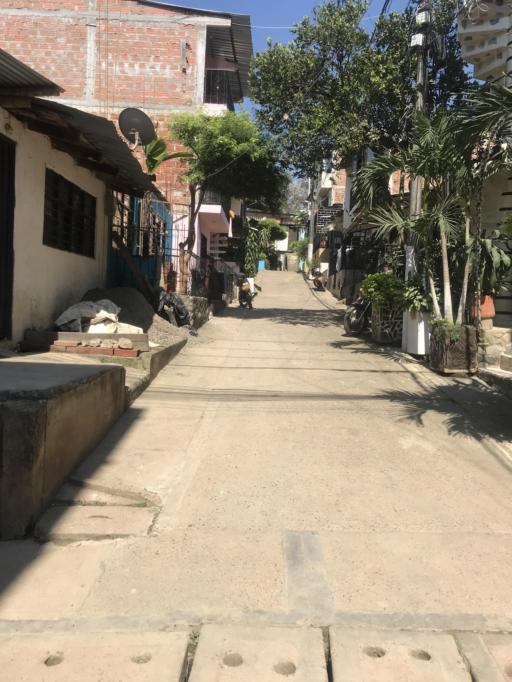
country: CO
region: Valle del Cauca
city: Cali
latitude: 3.3776
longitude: -76.5594
